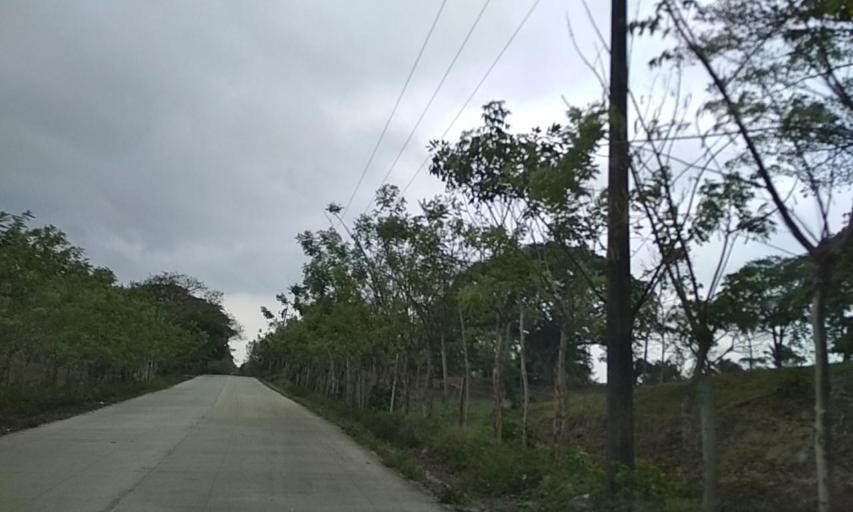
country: MX
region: Tabasco
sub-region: Huimanguillo
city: Francisco Rueda
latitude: 17.6472
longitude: -94.0932
